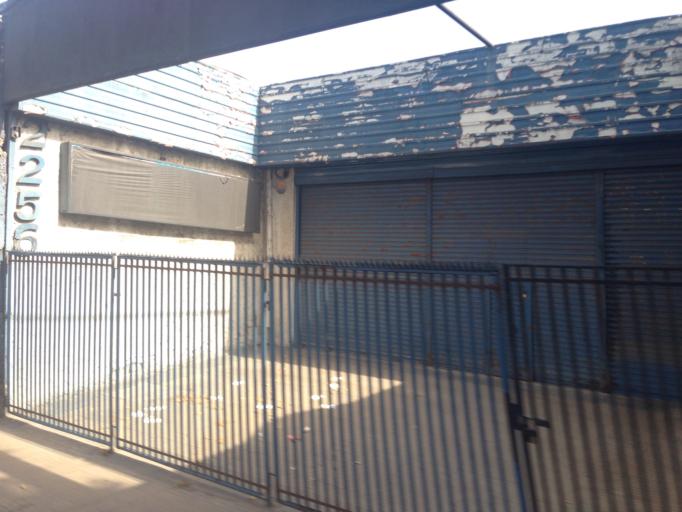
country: CL
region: Santiago Metropolitan
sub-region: Provincia de Santiago
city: Villa Presidente Frei, Nunoa, Santiago, Chile
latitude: -33.4538
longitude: -70.6074
